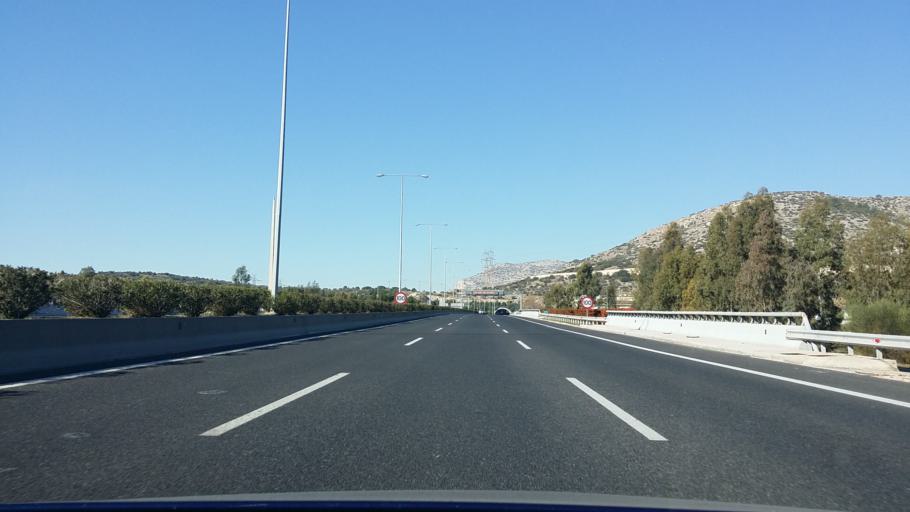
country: GR
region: Attica
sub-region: Nomarchia Dytikis Attikis
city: Ano Liosia
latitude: 38.0778
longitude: 23.6796
